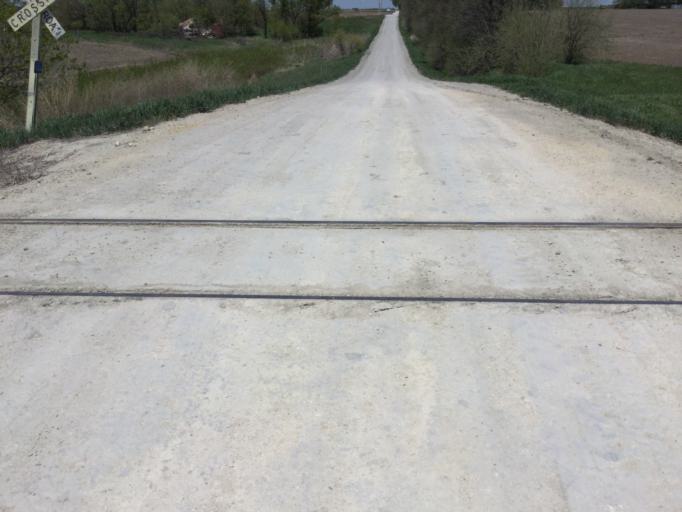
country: US
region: Kansas
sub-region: Smith County
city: Smith Center
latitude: 39.7745
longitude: -98.7669
